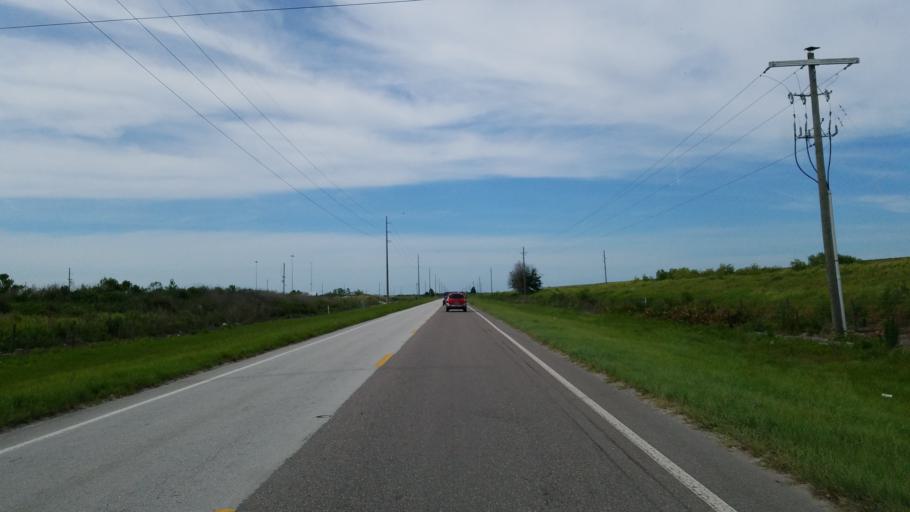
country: US
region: Florida
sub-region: Hillsborough County
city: Balm
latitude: 27.6498
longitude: -82.1463
